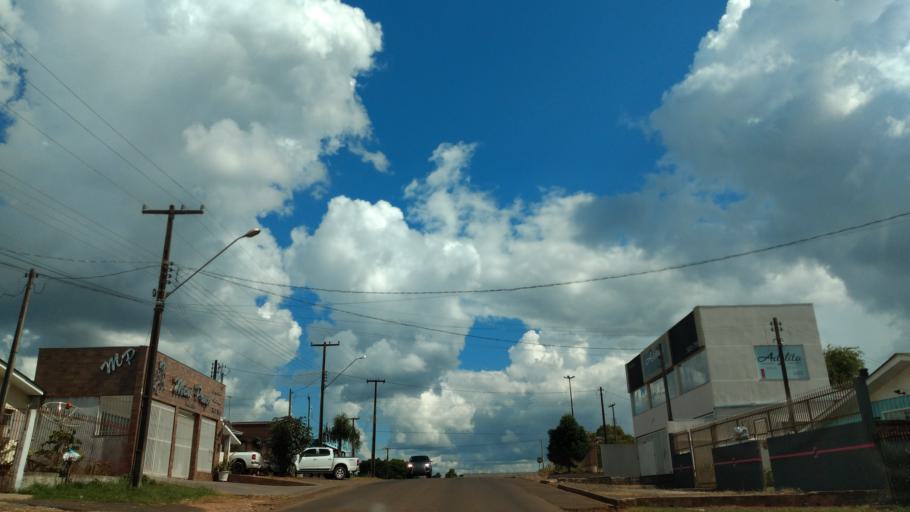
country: BR
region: Parana
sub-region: Guarapuava
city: Guarapuava
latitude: -25.4113
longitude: -51.4926
